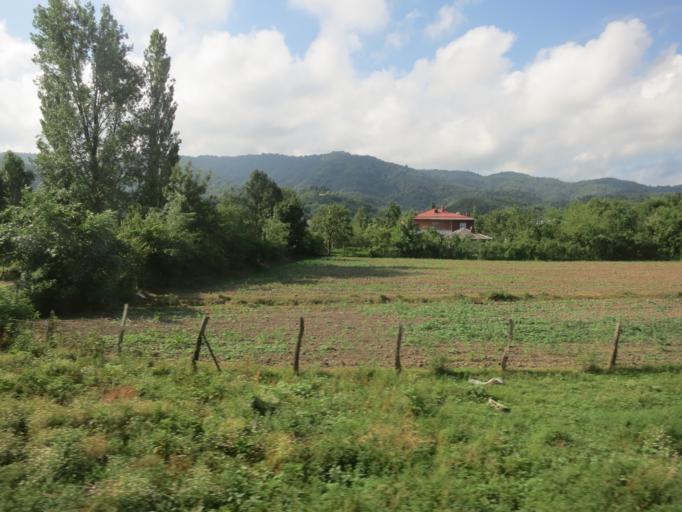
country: GE
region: Guria
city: Lanchkhuti
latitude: 42.0873
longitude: 42.1050
